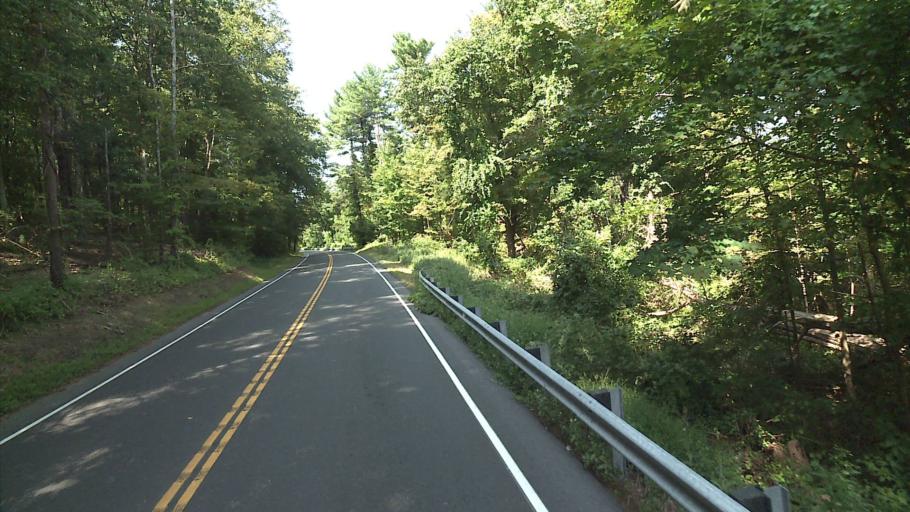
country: US
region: Connecticut
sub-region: Fairfield County
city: Southport
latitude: 41.2156
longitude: -73.2921
